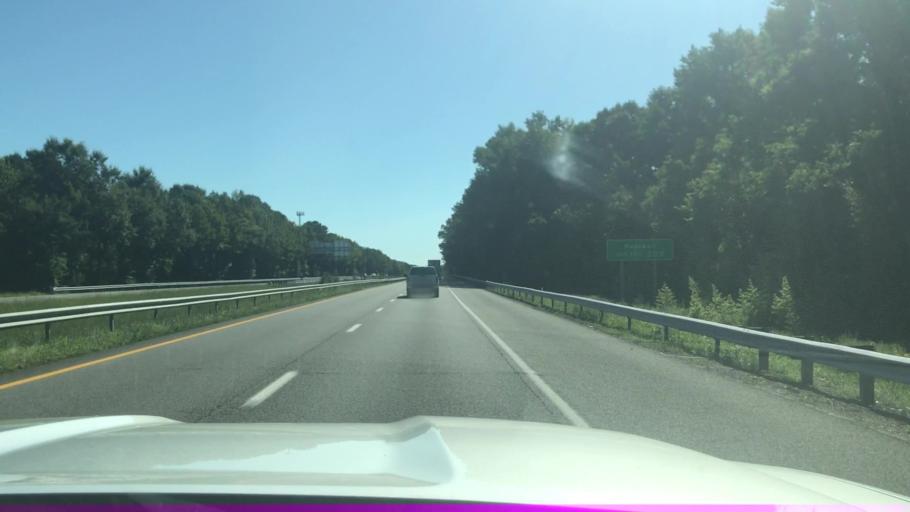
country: US
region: Virginia
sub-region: Henrico County
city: Sandston
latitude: 37.5296
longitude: -77.3172
